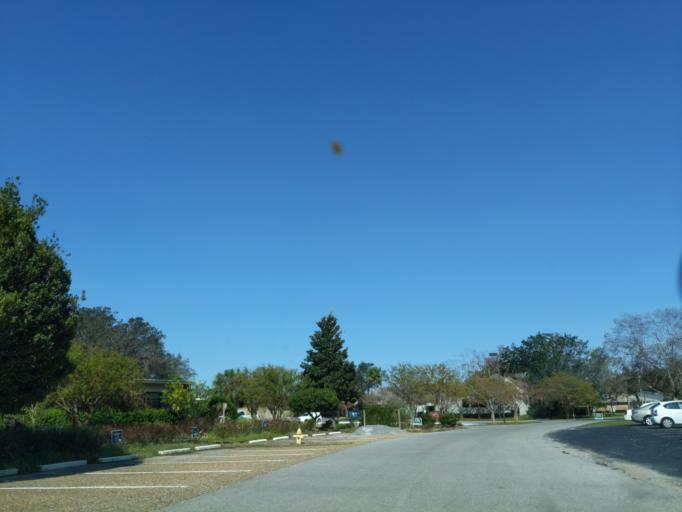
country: US
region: Florida
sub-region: Santa Rosa County
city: Gulf Breeze
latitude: 30.3633
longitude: -87.1726
